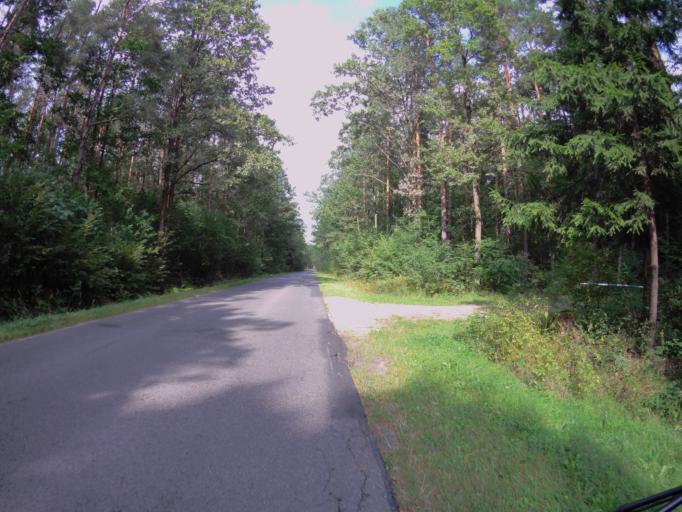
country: PL
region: Subcarpathian Voivodeship
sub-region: Powiat lezajski
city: Brzoza Krolewska
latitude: 50.2584
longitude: 22.3669
